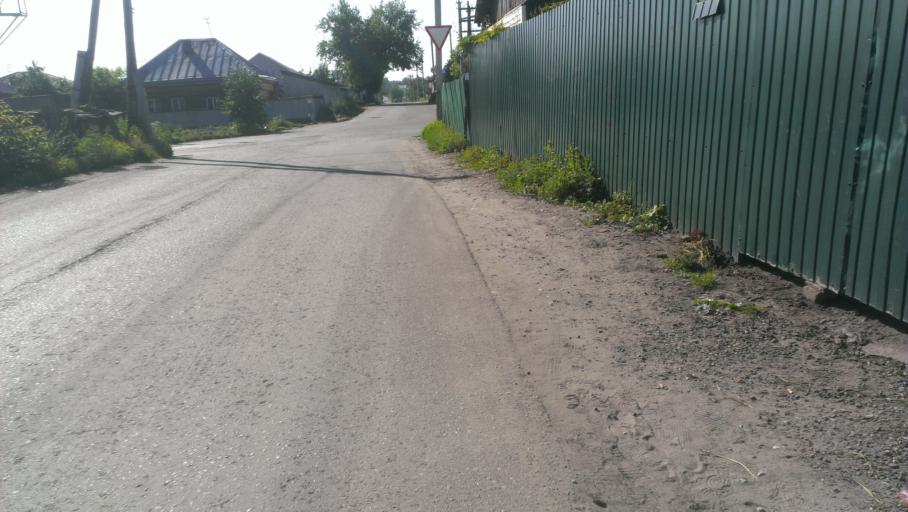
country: RU
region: Altai Krai
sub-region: Gorod Barnaulskiy
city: Barnaul
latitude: 53.3560
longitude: 83.7486
